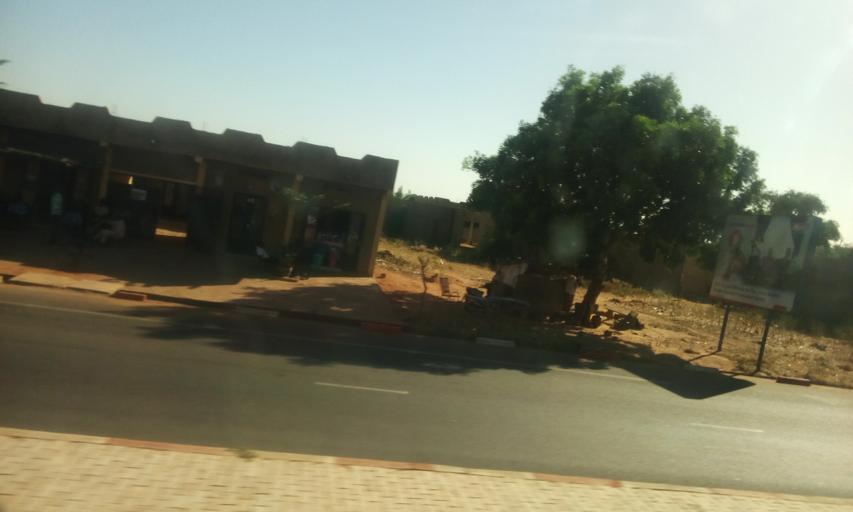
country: ML
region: Segou
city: Segou
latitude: 13.4146
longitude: -6.3217
